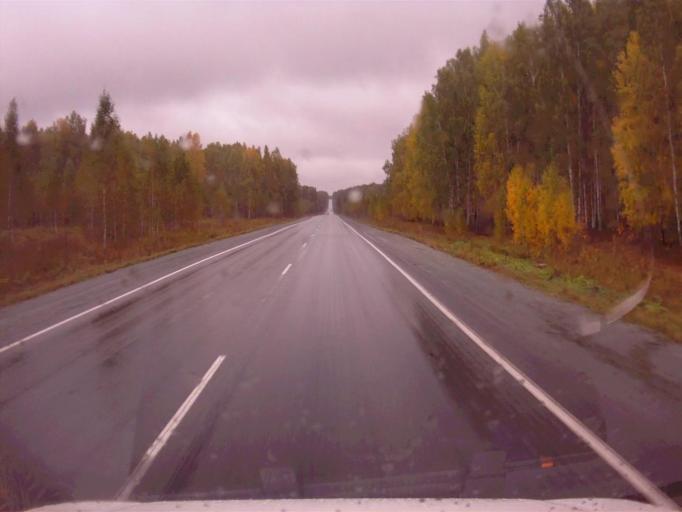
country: RU
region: Chelyabinsk
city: Tayginka
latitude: 55.5124
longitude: 60.6391
